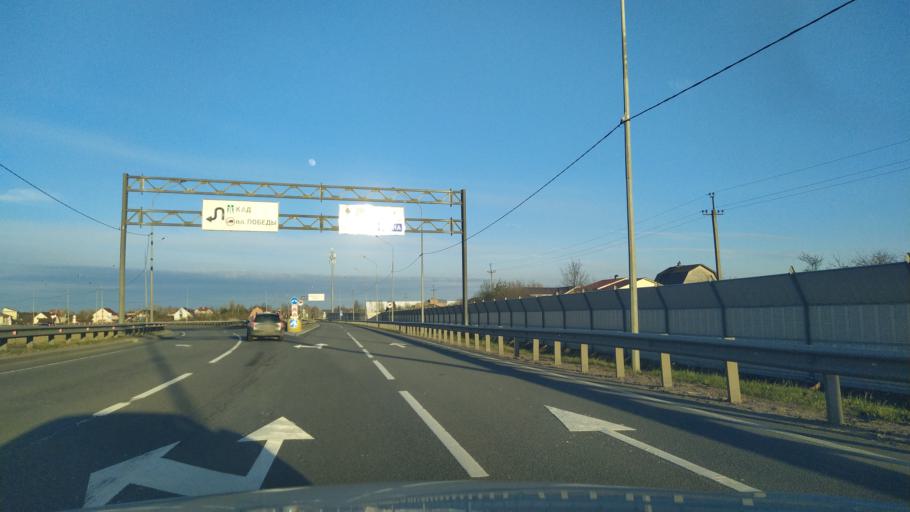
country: RU
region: St.-Petersburg
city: Aleksandrovskaya
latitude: 59.7407
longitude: 30.3200
